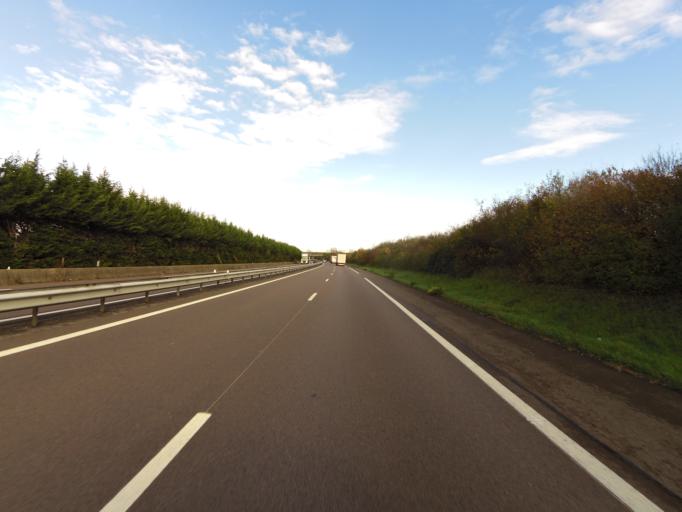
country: FR
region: Bourgogne
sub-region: Departement de la Cote-d'Or
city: Ouges
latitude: 47.2458
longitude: 5.1031
